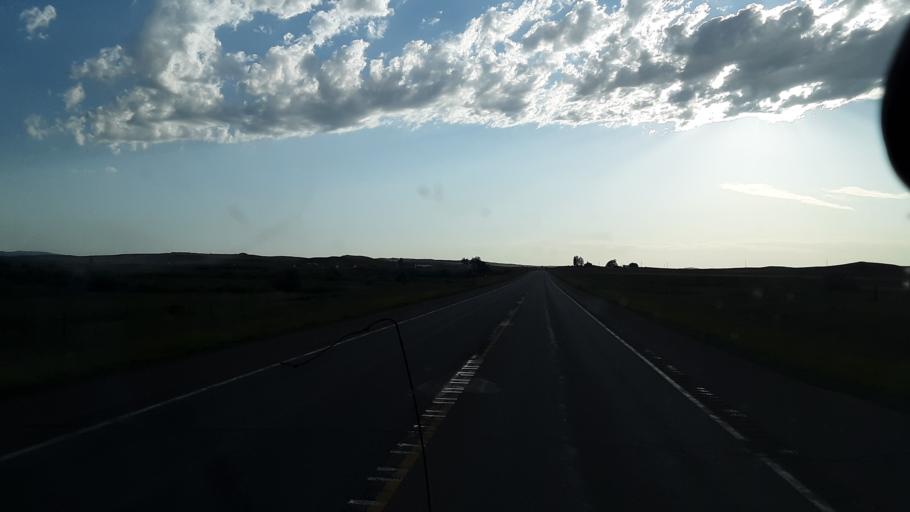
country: US
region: Montana
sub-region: Rosebud County
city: Lame Deer
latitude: 45.5283
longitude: -106.9660
